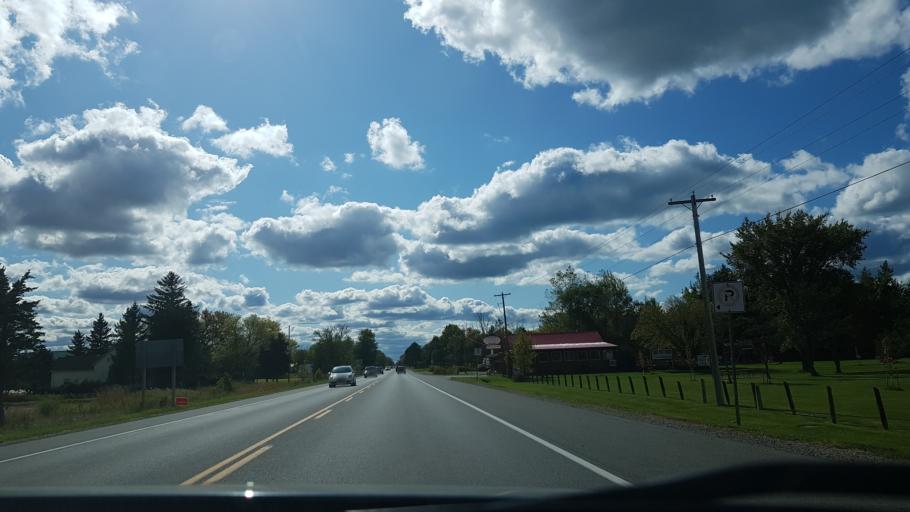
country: CA
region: Ontario
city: Bluewater
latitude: 43.3335
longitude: -81.7395
